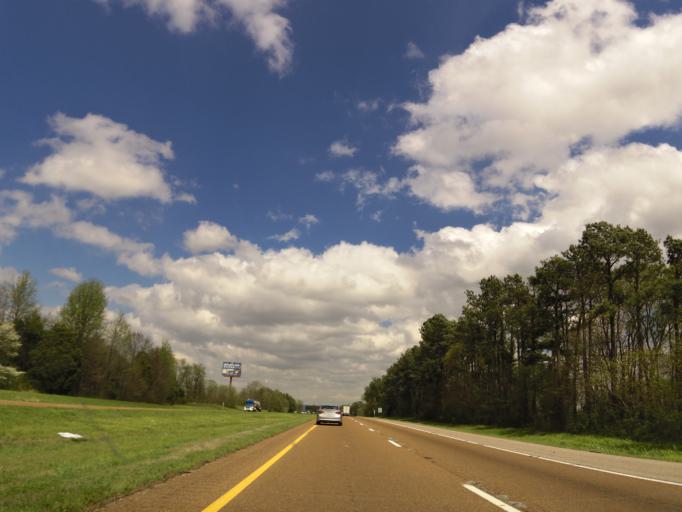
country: US
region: Tennessee
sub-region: Tipton County
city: Mason
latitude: 35.3520
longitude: -89.5112
